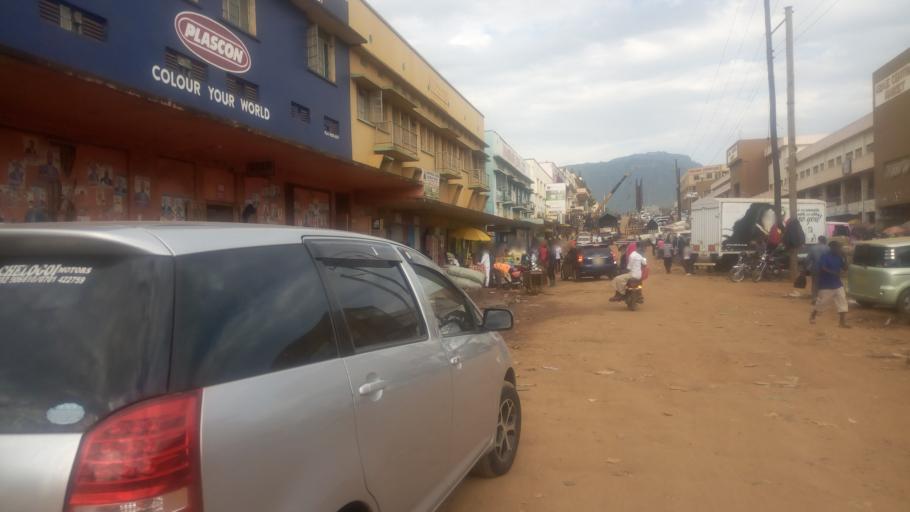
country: UG
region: Eastern Region
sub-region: Mbale District
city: Mbale
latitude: 1.0718
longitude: 34.1777
